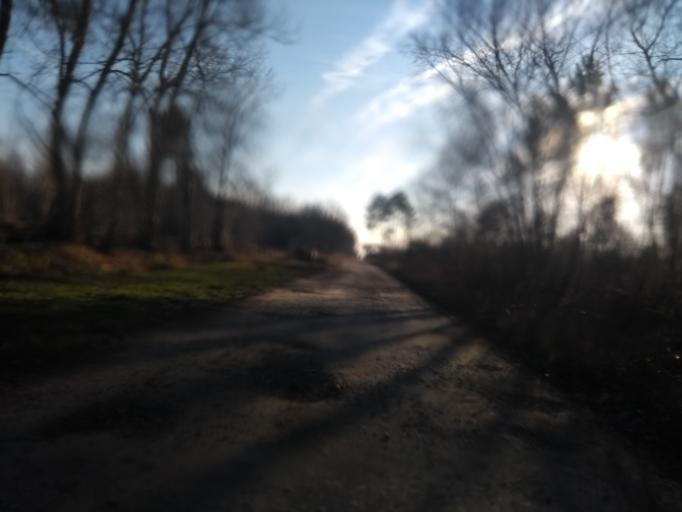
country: FR
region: Aquitaine
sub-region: Departement de la Gironde
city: Le Barp
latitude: 44.6028
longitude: -0.7946
